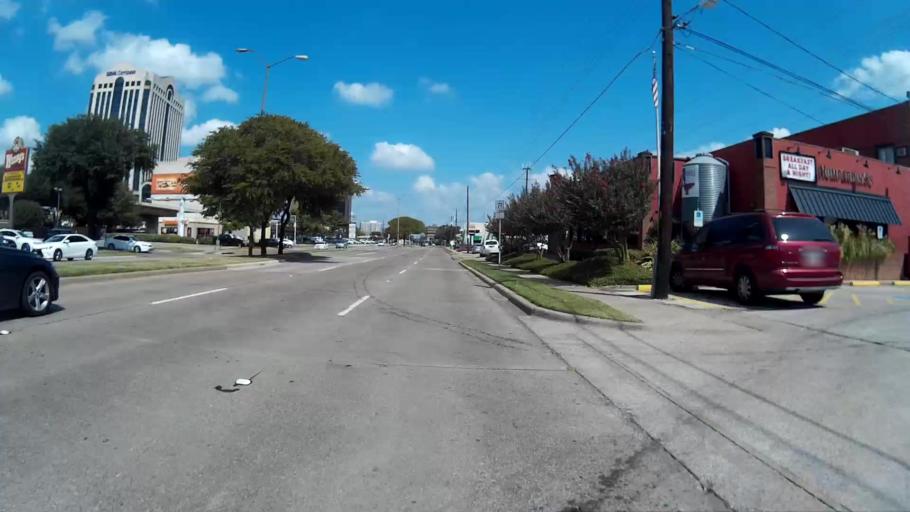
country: US
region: Texas
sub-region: Dallas County
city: University Park
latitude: 32.8583
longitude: -96.7683
